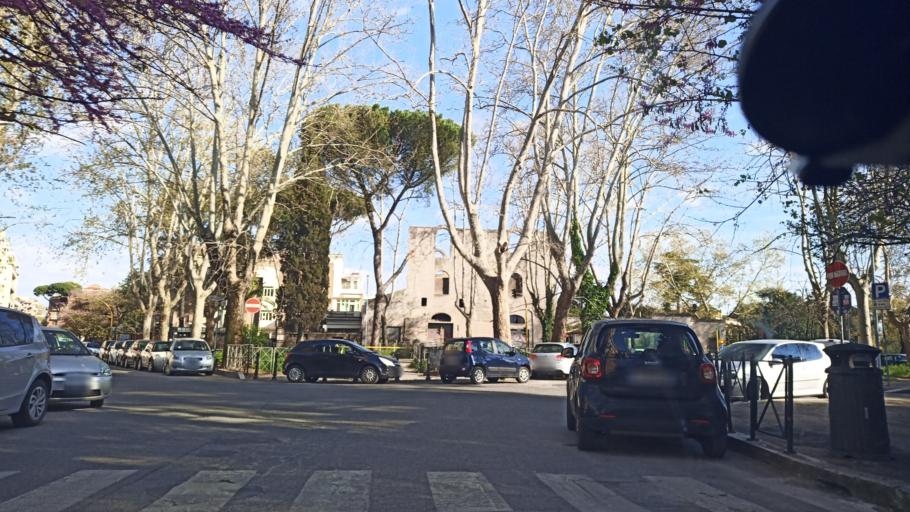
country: IT
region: Latium
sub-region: Citta metropolitana di Roma Capitale
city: Rome
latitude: 41.8748
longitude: 12.5059
